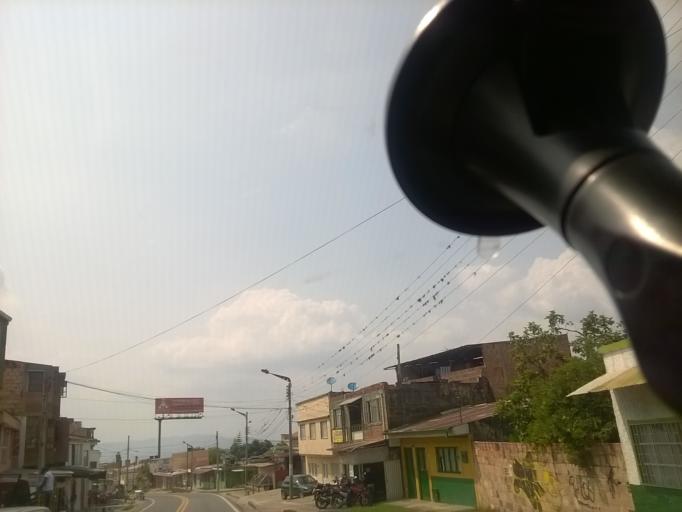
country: CO
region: Cundinamarca
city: San Antonio del Tequendama
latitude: 4.6307
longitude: -74.4591
